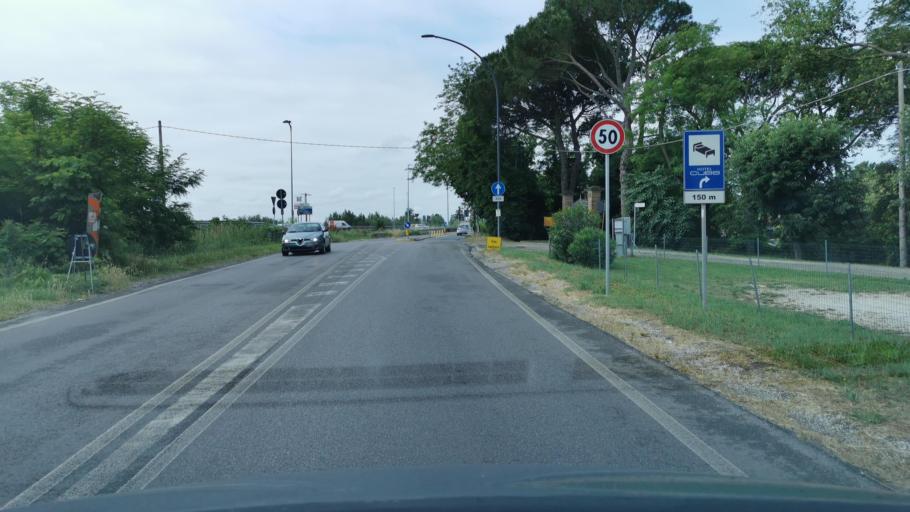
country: IT
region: Emilia-Romagna
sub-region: Provincia di Ravenna
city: Madonna Dell'Albero
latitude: 44.3859
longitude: 12.1958
